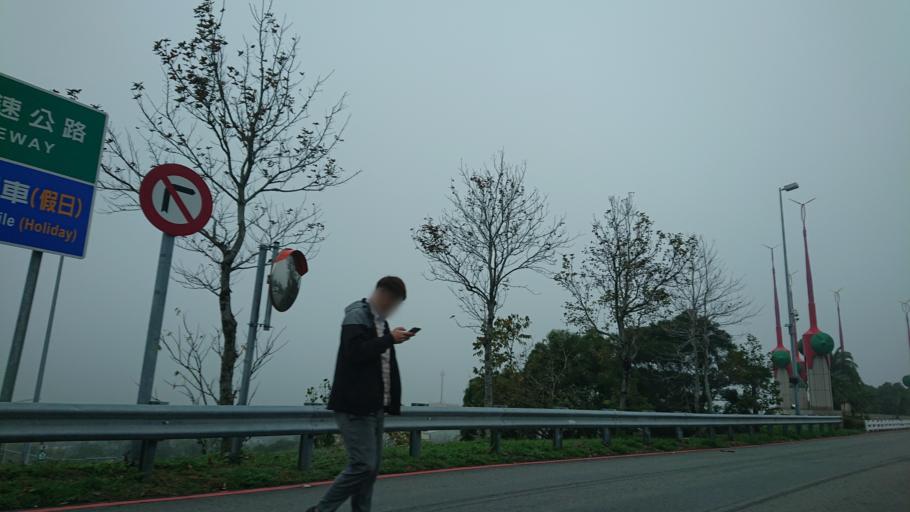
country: TW
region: Taiwan
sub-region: Miaoli
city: Miaoli
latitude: 24.5653
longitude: 120.7587
